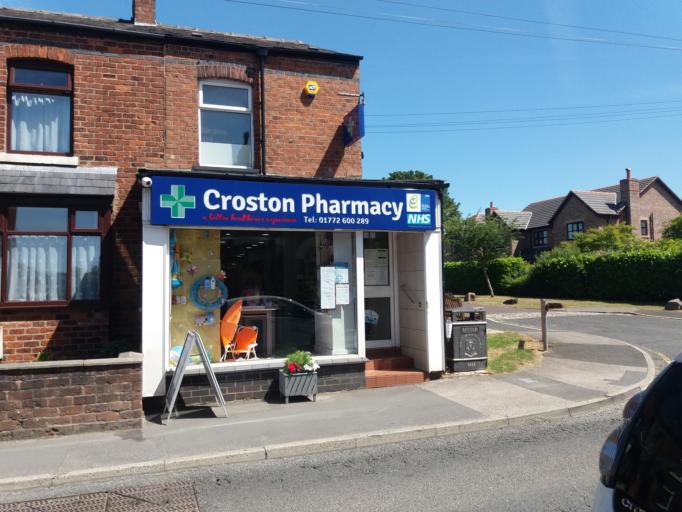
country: GB
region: England
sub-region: Lancashire
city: Croston
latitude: 53.6650
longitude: -2.7759
